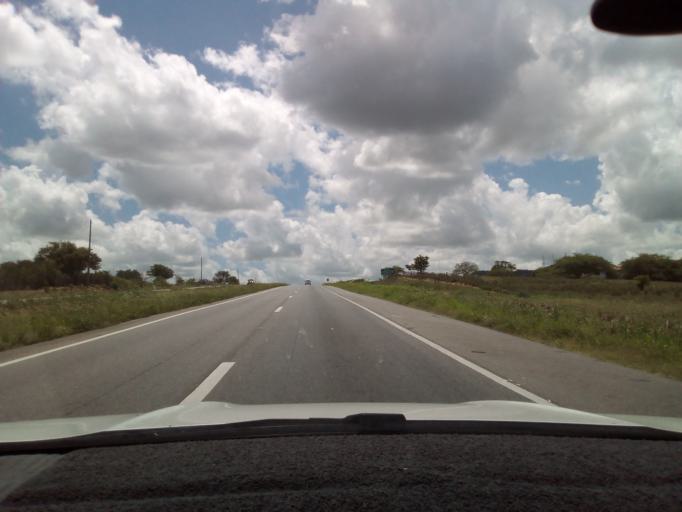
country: BR
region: Paraiba
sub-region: Gurinhem
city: Gurinhem
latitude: -7.1836
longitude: -35.4403
